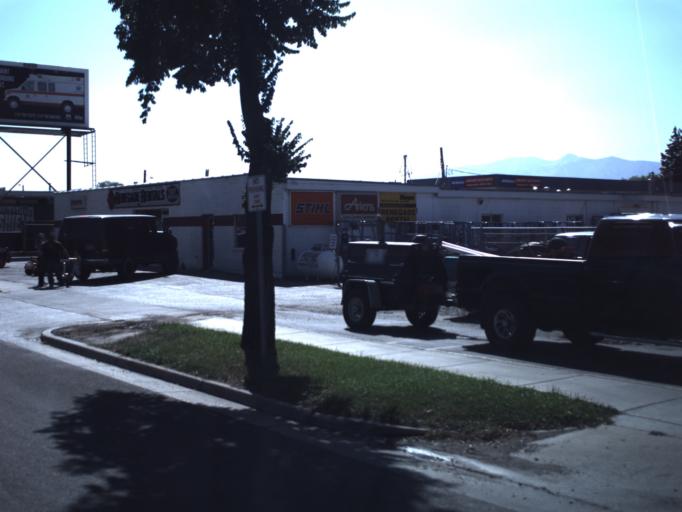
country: US
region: Utah
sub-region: Cache County
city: Logan
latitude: 41.7491
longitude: -111.8346
